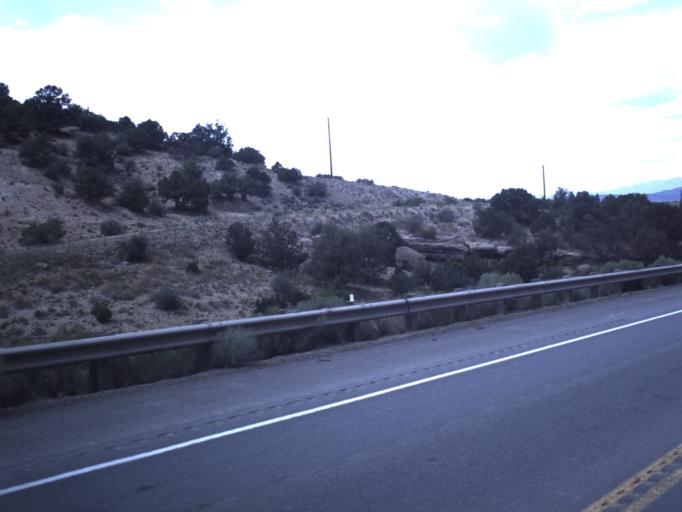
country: US
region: Utah
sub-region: Duchesne County
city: Duchesne
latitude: 40.1693
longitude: -110.4856
